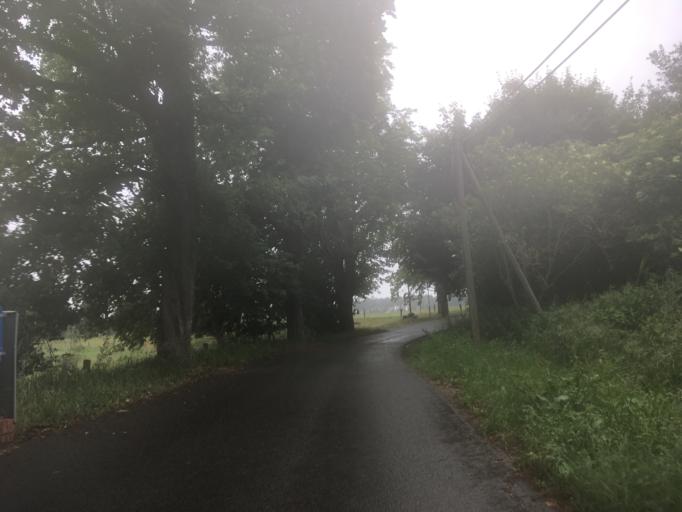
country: DE
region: Brandenburg
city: Liebenwalde
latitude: 52.8760
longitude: 13.3809
